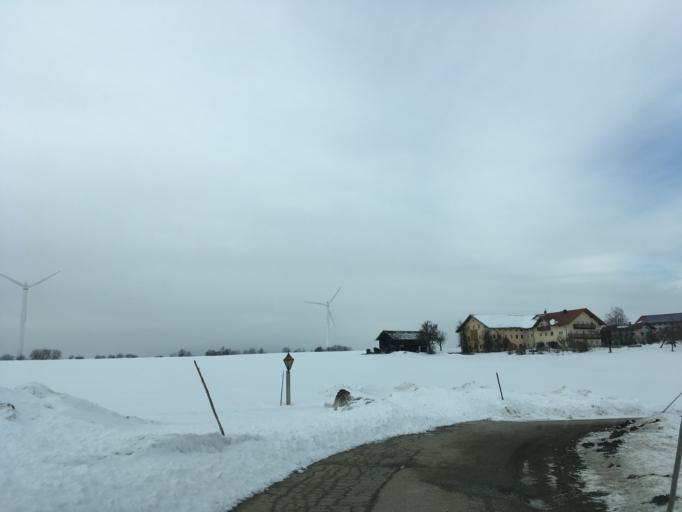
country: DE
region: Bavaria
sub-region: Upper Bavaria
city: Schnaitsee
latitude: 48.0793
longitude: 12.3682
